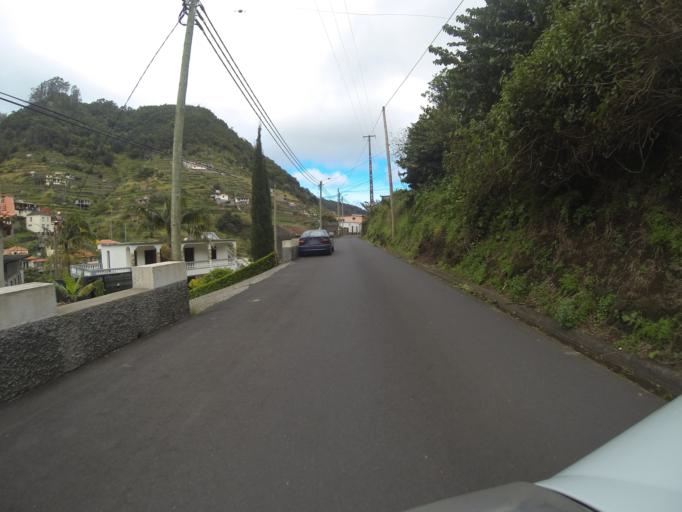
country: PT
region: Madeira
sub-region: Machico
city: Machico
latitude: 32.7352
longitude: -16.7933
